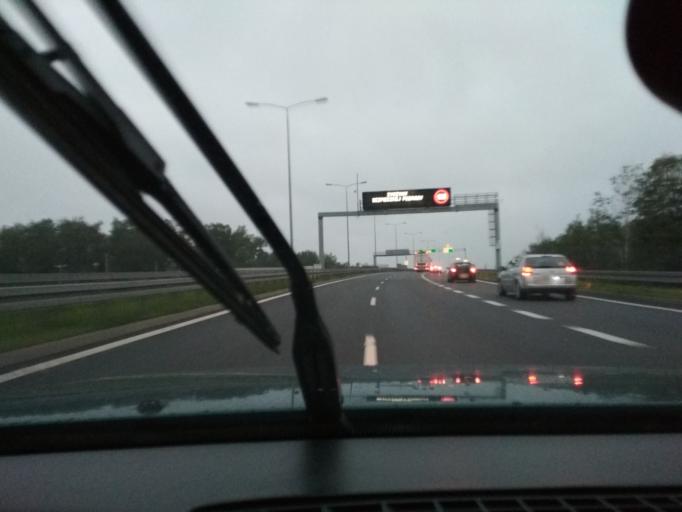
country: PL
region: Silesian Voivodeship
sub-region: Gliwice
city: Gliwice
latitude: 50.2810
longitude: 18.7157
